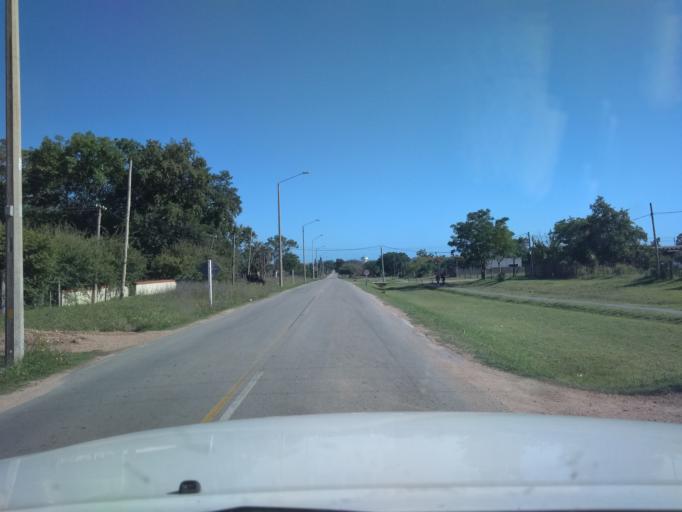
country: UY
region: Canelones
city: San Ramon
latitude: -34.3039
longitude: -55.9581
